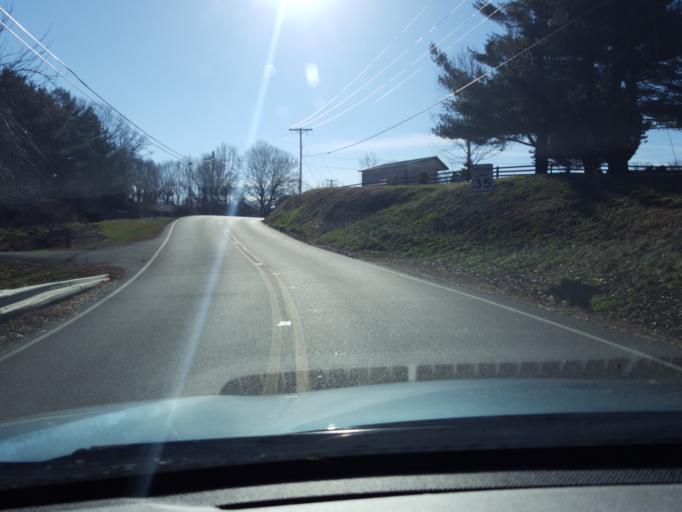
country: US
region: Maryland
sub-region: Calvert County
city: Huntingtown Town Center
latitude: 38.6614
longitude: -76.5897
